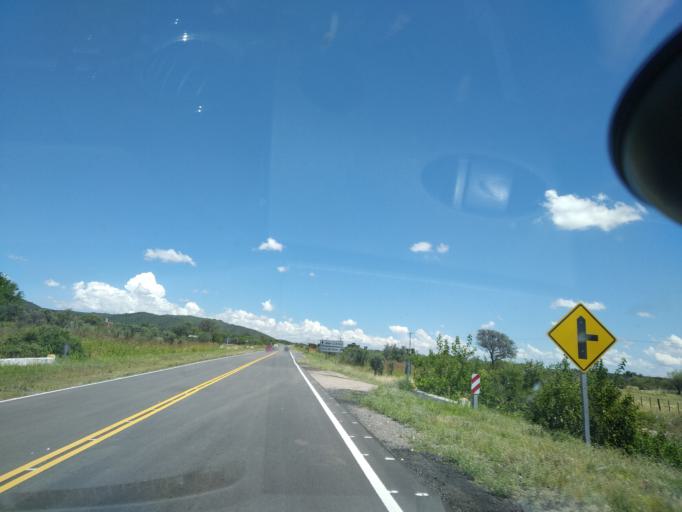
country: AR
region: Cordoba
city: Salsacate
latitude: -31.3664
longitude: -65.1057
